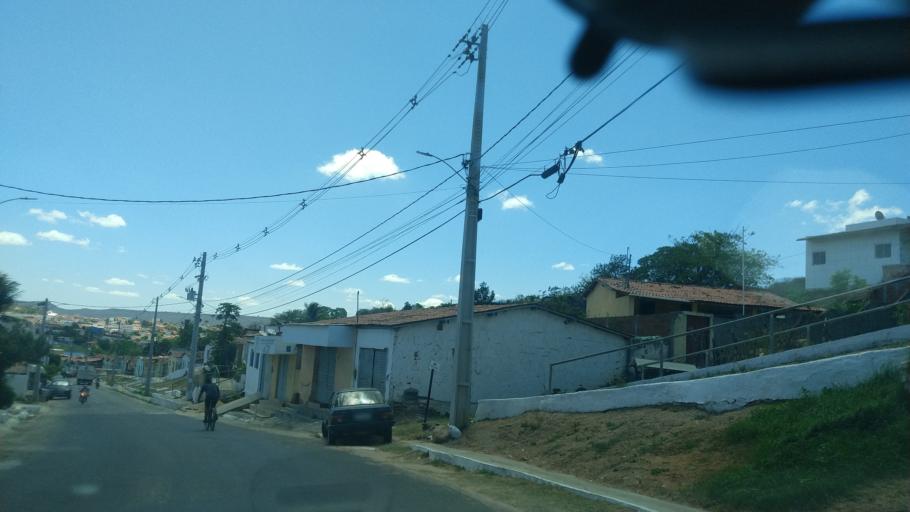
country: BR
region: Rio Grande do Norte
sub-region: Cerro Cora
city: Cerro Cora
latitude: -6.0364
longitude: -36.3471
